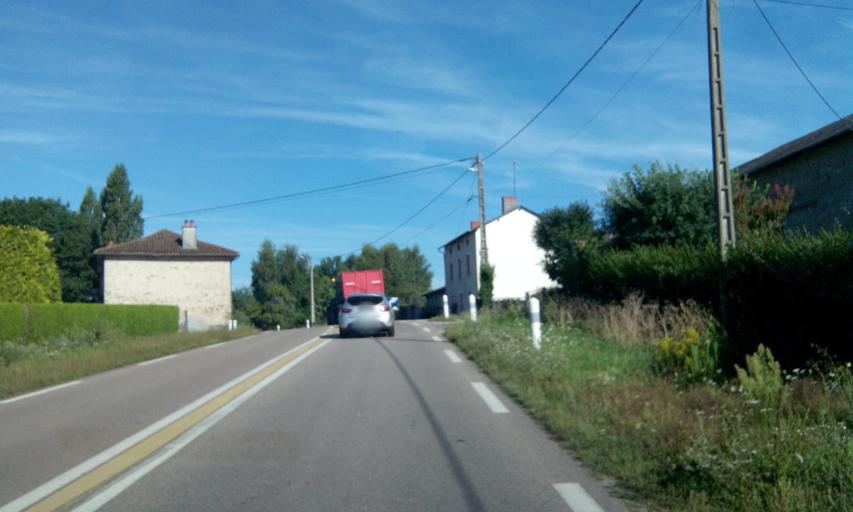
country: FR
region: Limousin
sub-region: Departement de la Haute-Vienne
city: Saint-Leonard-de-Noblat
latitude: 45.8463
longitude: 1.4576
